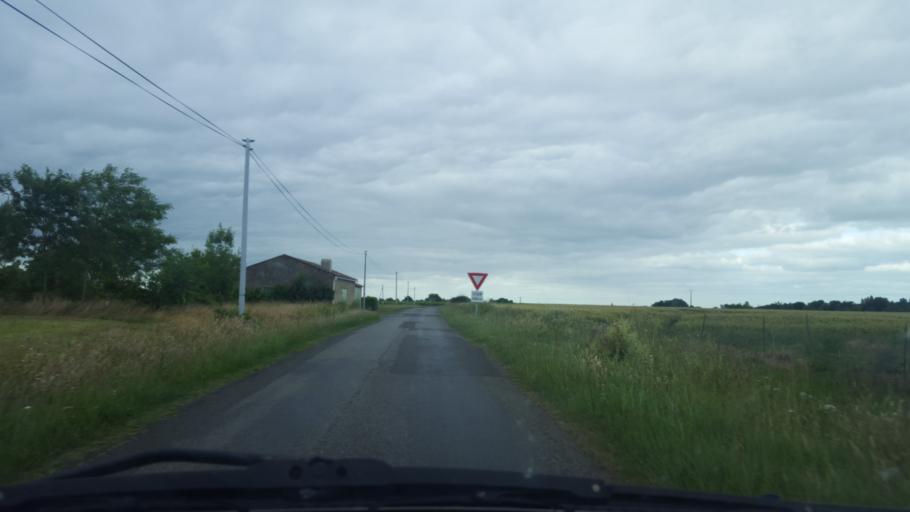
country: FR
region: Pays de la Loire
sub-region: Departement de la Loire-Atlantique
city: Saint-Philbert-de-Grand-Lieu
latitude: 47.0195
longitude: -1.6727
